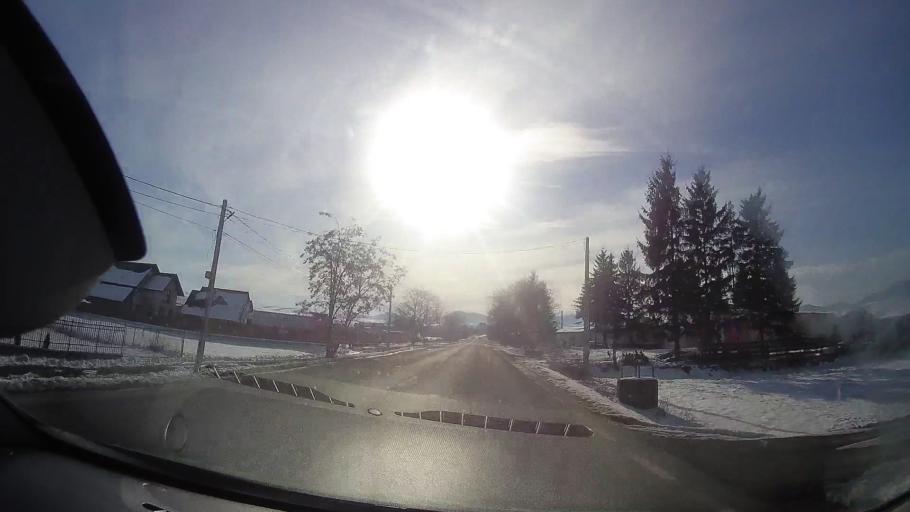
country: RO
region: Neamt
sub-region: Comuna Baltatesti
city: Valea Seaca
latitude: 47.1433
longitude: 26.3191
